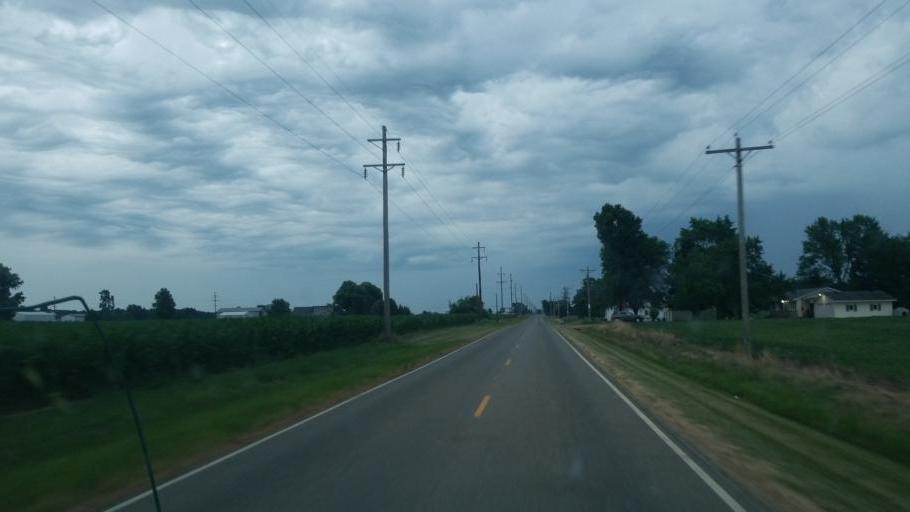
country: US
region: Ohio
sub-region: Defiance County
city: Hicksville
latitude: 41.3572
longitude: -84.7670
